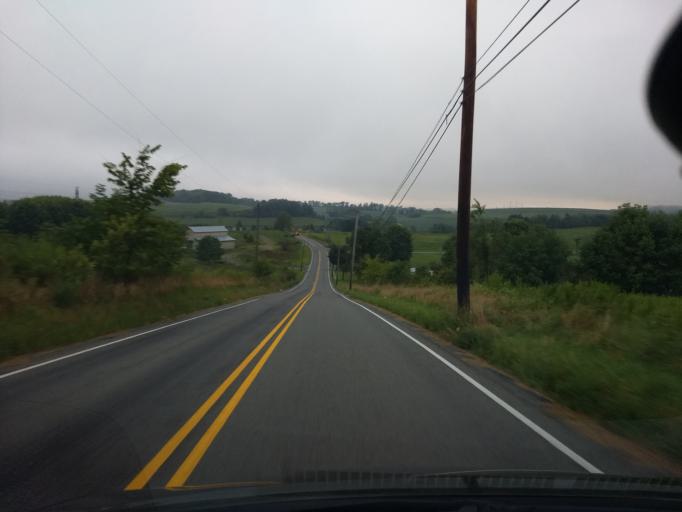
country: US
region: Pennsylvania
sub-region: Westmoreland County
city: Greensburg
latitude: 40.3246
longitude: -79.4883
